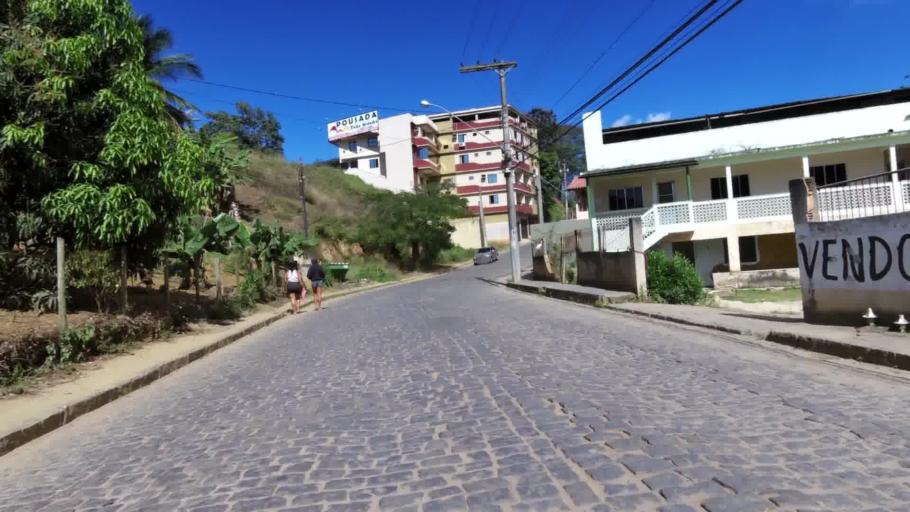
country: BR
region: Espirito Santo
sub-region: Rio Novo Do Sul
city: Rio Novo do Sul
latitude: -20.8652
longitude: -40.9366
